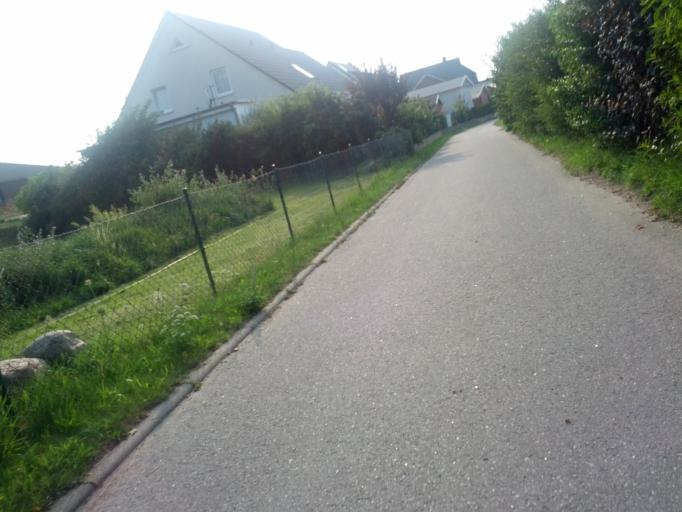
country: DE
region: Mecklenburg-Vorpommern
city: Ostseebad Kuhlungsborn
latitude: 54.1447
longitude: 11.7329
